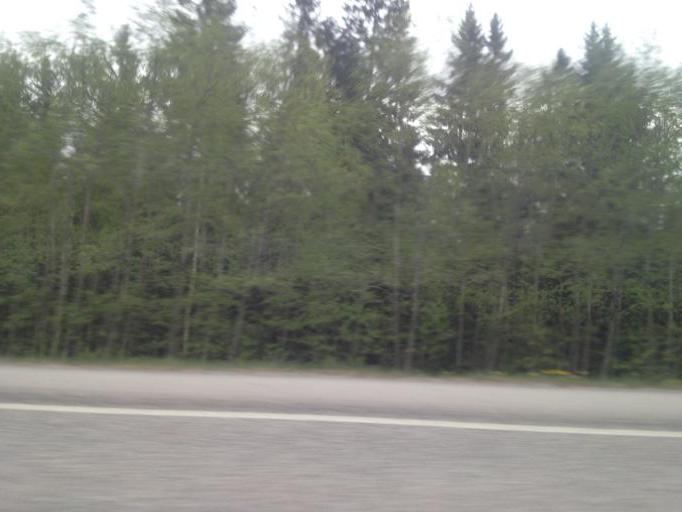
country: FI
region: Uusimaa
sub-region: Helsinki
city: Nurmijaervi
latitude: 60.4478
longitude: 24.8424
